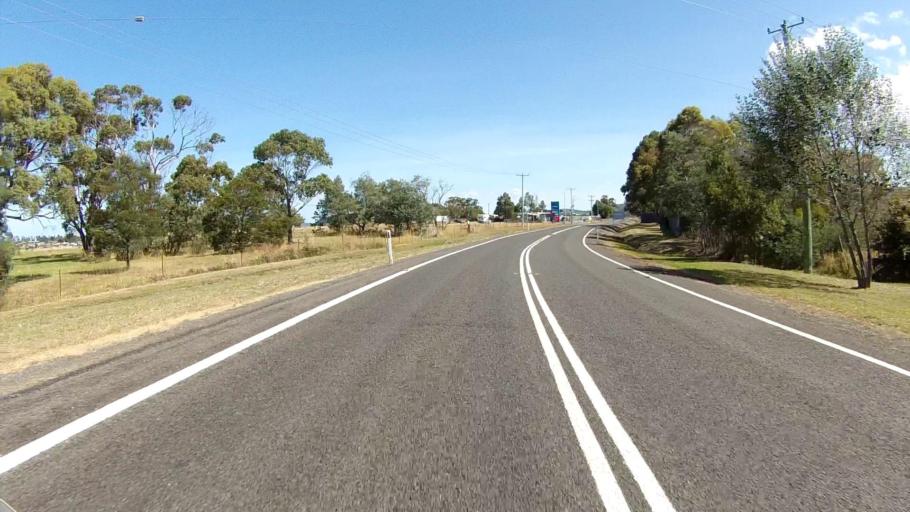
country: AU
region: Tasmania
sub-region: Sorell
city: Sorell
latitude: -42.4995
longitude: 147.9206
